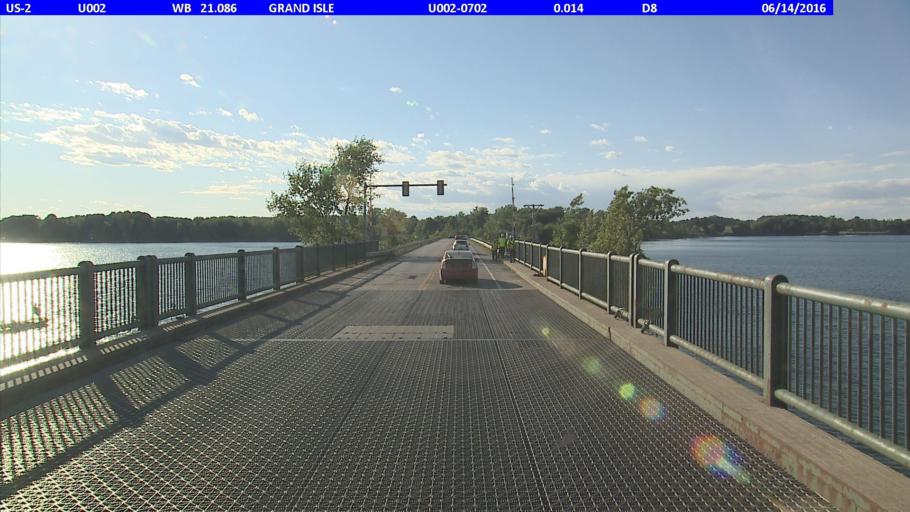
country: US
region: Vermont
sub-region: Grand Isle County
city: North Hero
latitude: 44.7660
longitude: -73.2898
